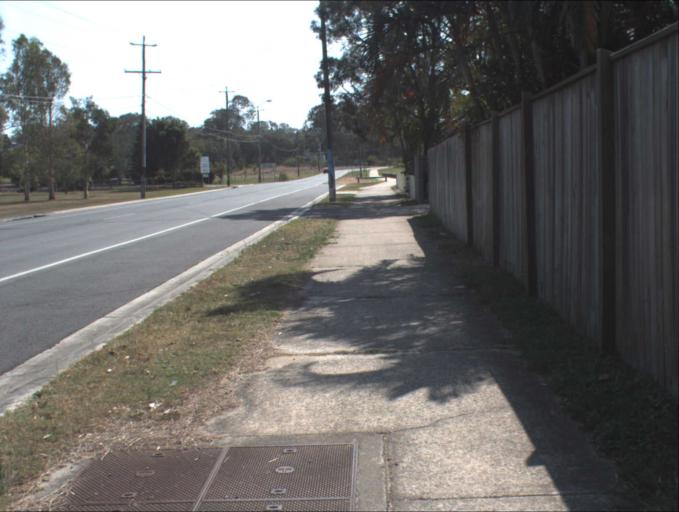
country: AU
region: Queensland
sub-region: Logan
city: Beenleigh
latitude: -27.6910
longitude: 153.1869
